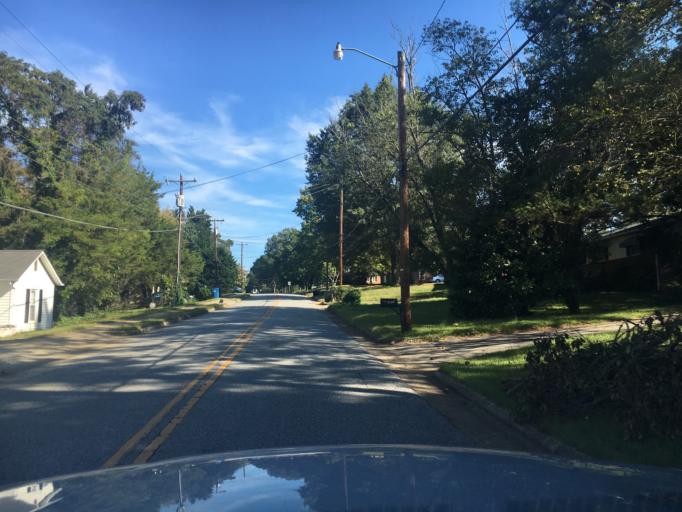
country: US
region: North Carolina
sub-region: Catawba County
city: Hickory
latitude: 35.7266
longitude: -81.3535
